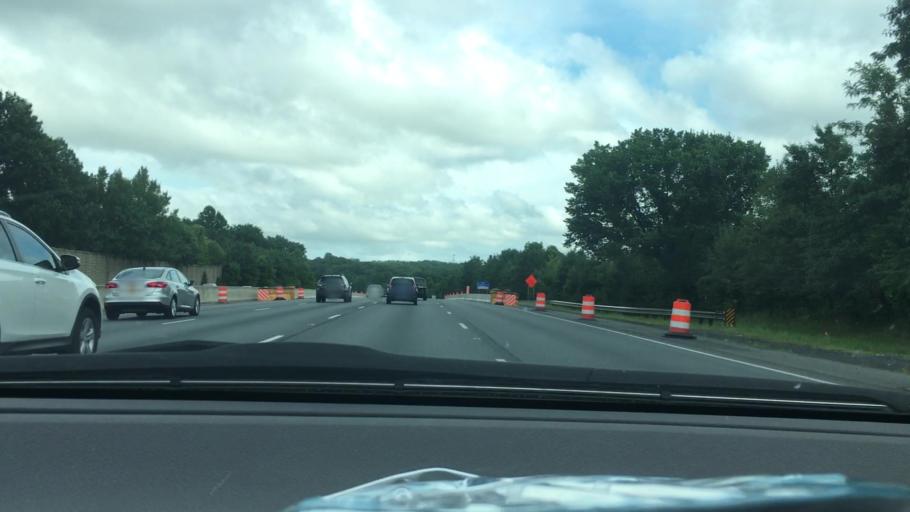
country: US
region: Maryland
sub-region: Montgomery County
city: Germantown
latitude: 39.1707
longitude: -77.2442
